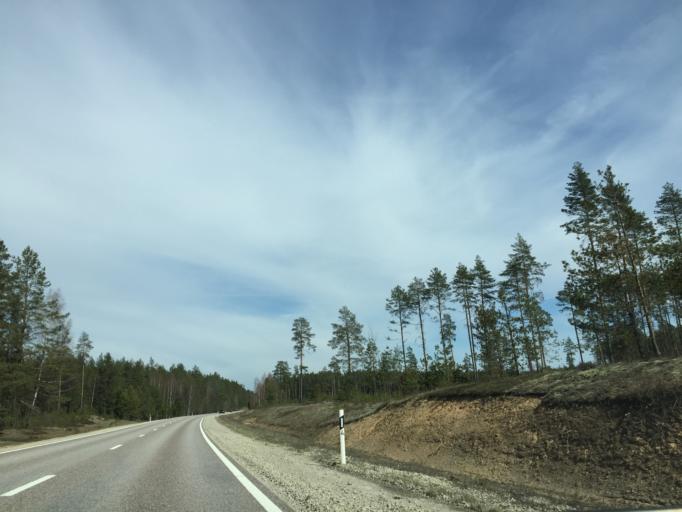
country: LV
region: Strenci
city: Seda
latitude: 57.6693
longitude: 25.8776
